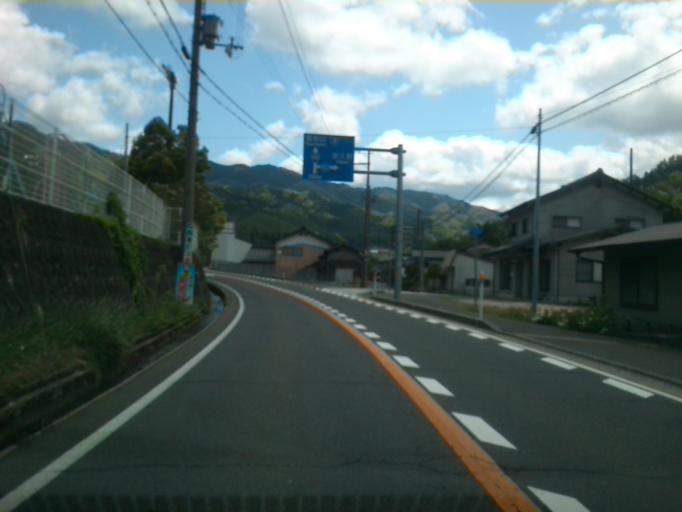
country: JP
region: Kyoto
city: Fukuchiyama
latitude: 35.4205
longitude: 135.0075
